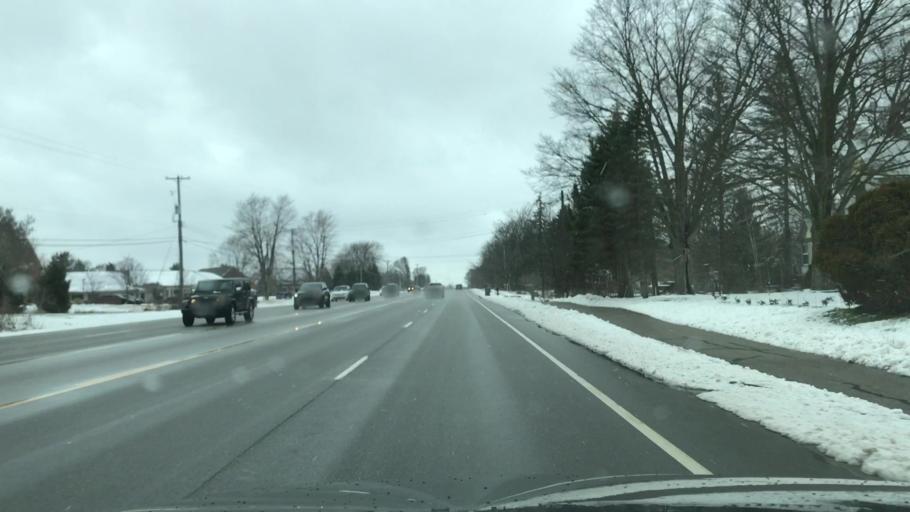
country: US
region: Michigan
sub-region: Kent County
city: Forest Hills
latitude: 42.9359
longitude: -85.5294
